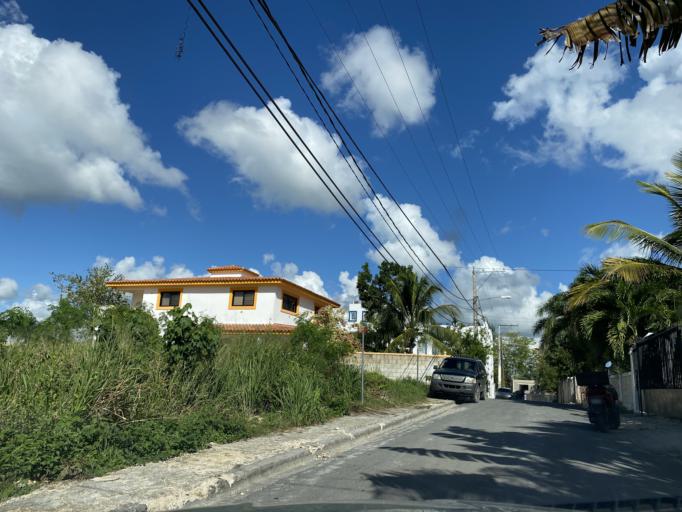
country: DO
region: La Romana
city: La Romana
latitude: 18.3694
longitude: -68.8360
